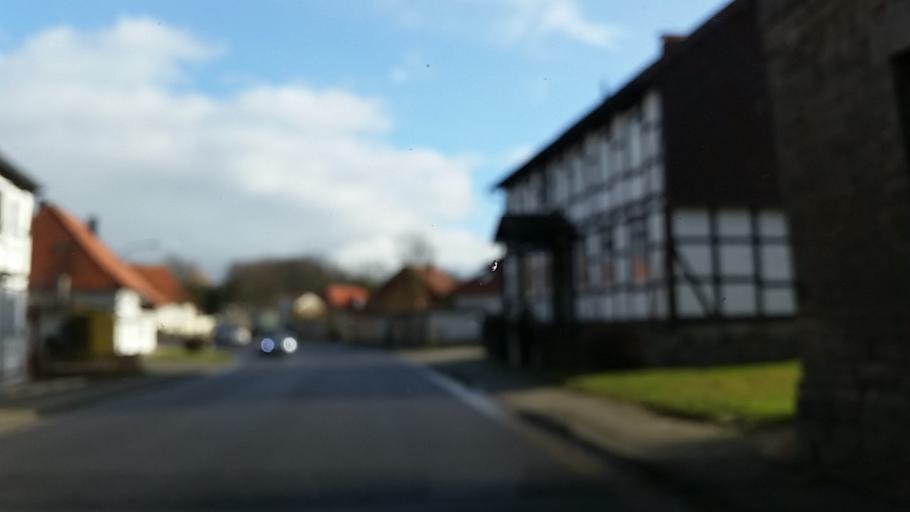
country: DE
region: Lower Saxony
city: Gross Twulpstedt
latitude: 52.3854
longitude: 10.9226
